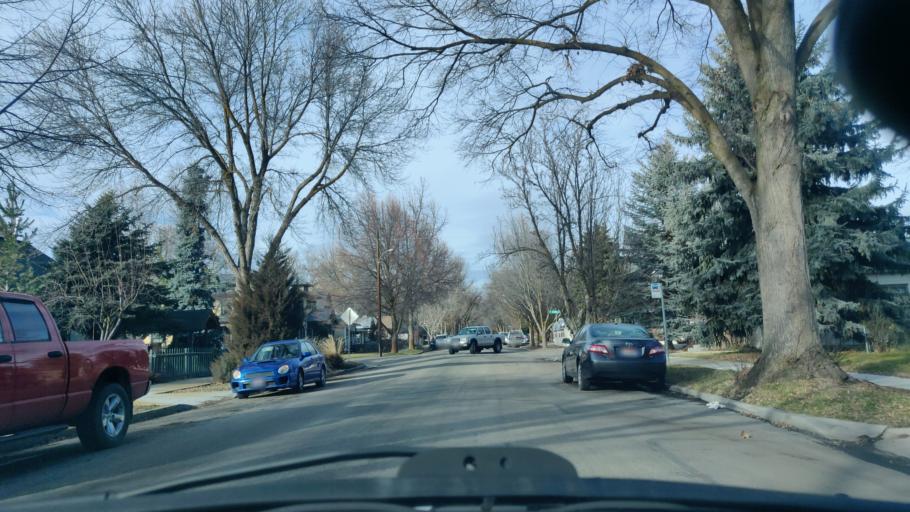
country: US
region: Idaho
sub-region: Ada County
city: Boise
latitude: 43.6306
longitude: -116.1987
